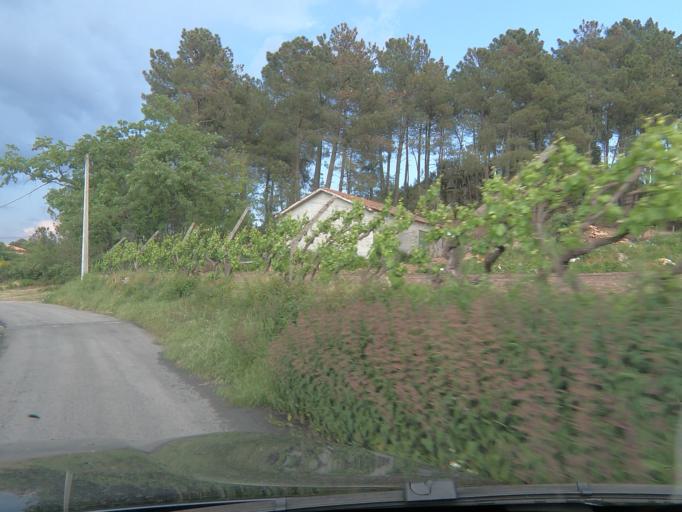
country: PT
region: Vila Real
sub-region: Vila Real
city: Vila Real
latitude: 41.3193
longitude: -7.6886
